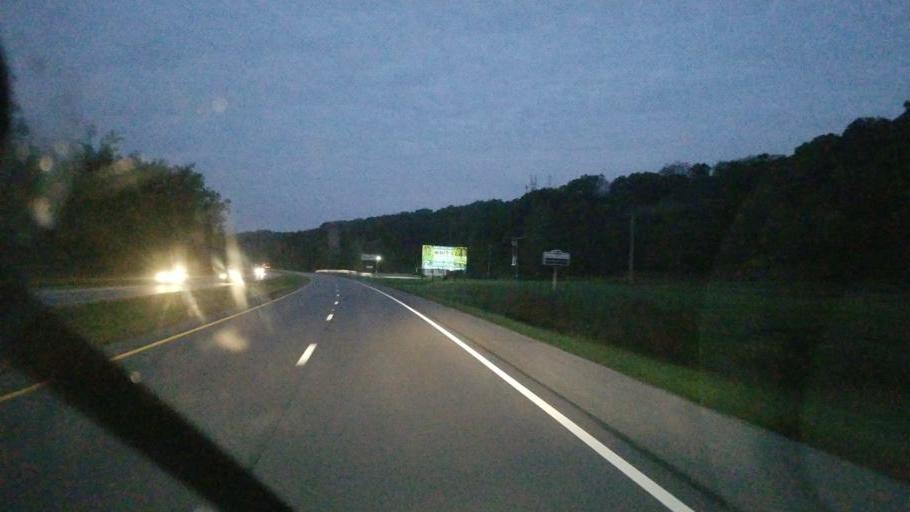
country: US
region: Ohio
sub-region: Ross County
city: Chillicothe
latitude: 39.2574
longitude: -82.9745
